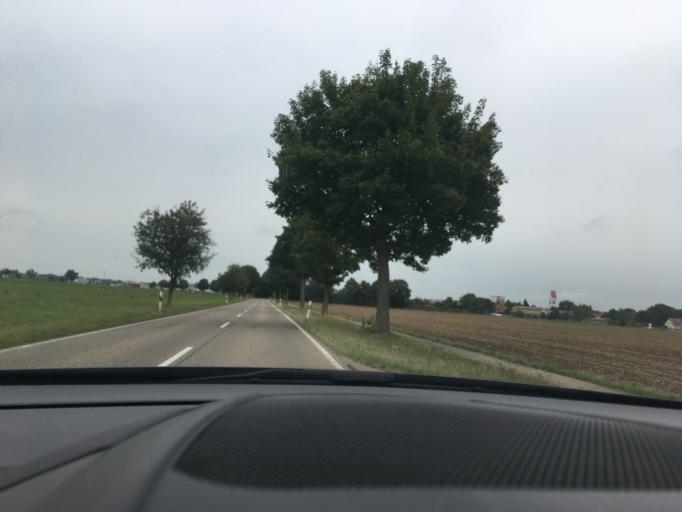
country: DE
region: Baden-Wuerttemberg
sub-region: Tuebingen Region
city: Kirchdorf
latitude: 48.0786
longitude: 10.1149
